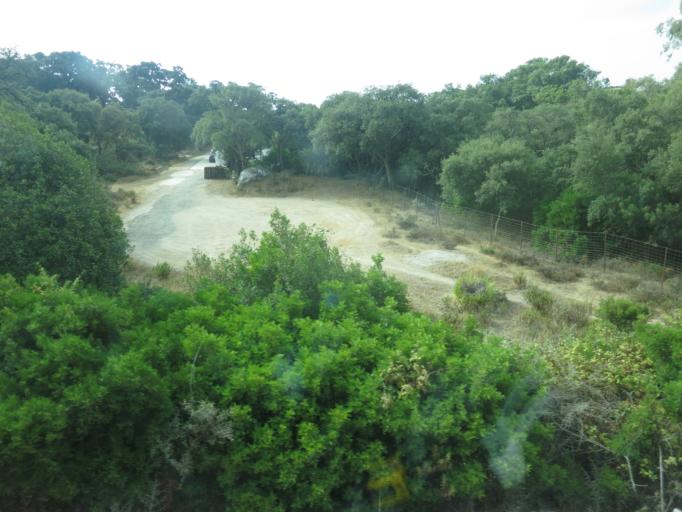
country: ES
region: Andalusia
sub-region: Provincia de Cadiz
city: Tarifa
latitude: 36.0695
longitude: -5.5295
